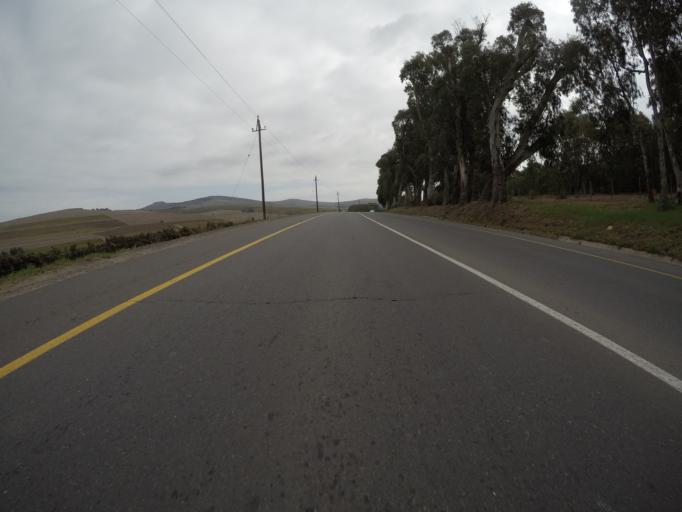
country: ZA
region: Western Cape
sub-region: City of Cape Town
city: Kraaifontein
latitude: -33.8427
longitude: 18.6214
